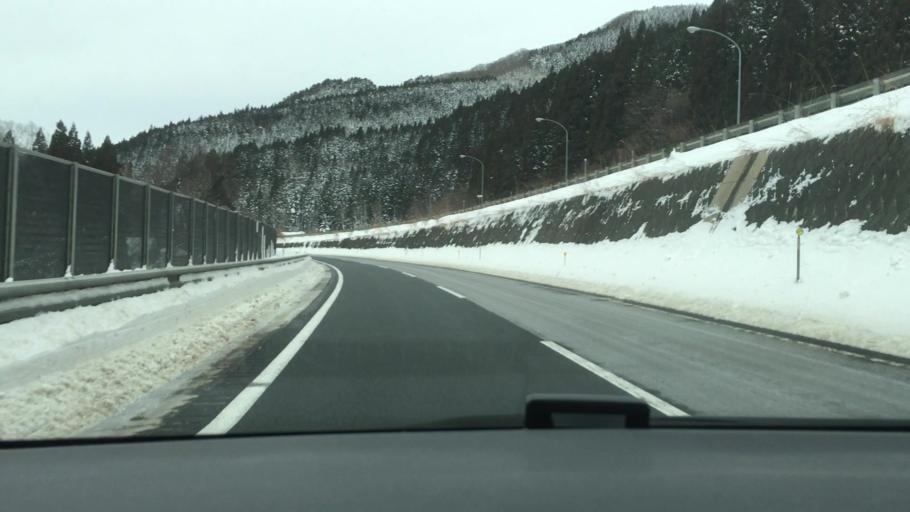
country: JP
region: Akita
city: Hanawa
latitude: 40.1245
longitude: 140.8397
